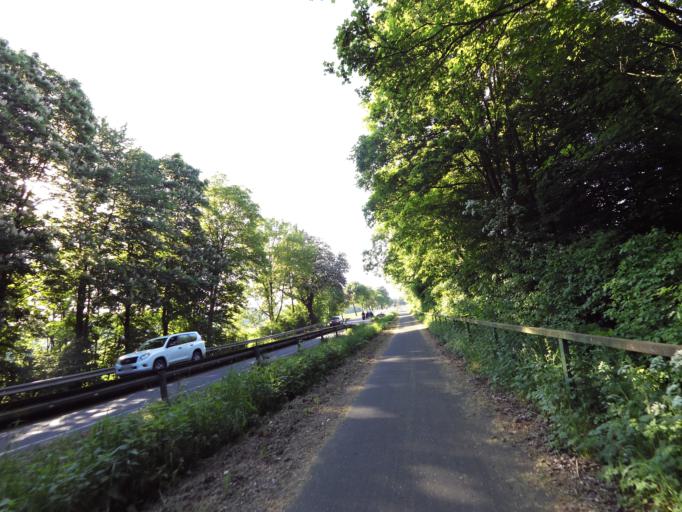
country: DE
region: North Rhine-Westphalia
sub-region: Regierungsbezirk Koln
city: Bonn
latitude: 50.6908
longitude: 7.0719
